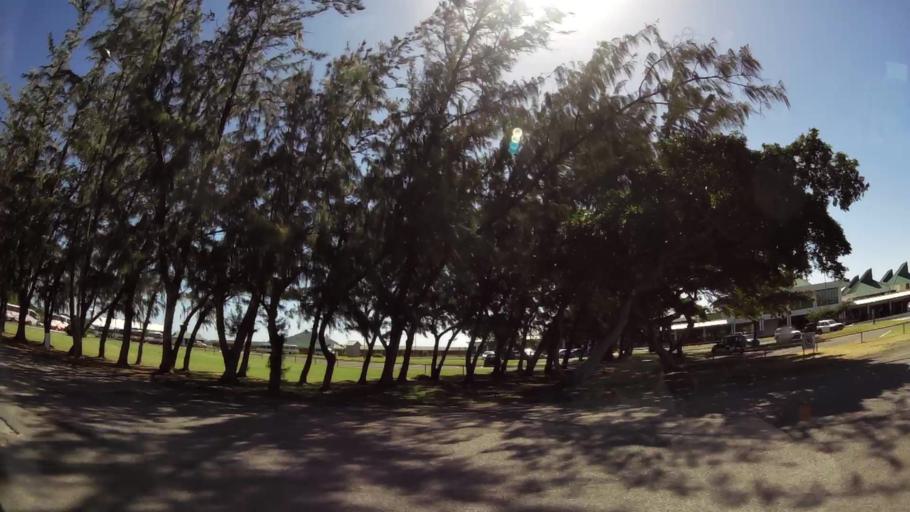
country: LC
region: Vieux-Fort
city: Vieux Fort
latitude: 13.7376
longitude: -60.9498
